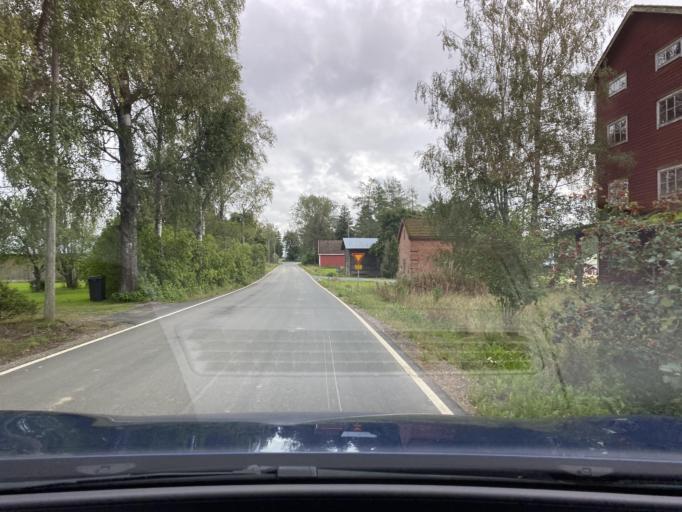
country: FI
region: Pirkanmaa
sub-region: Lounais-Pirkanmaa
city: Punkalaidun
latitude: 61.1664
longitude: 23.1844
